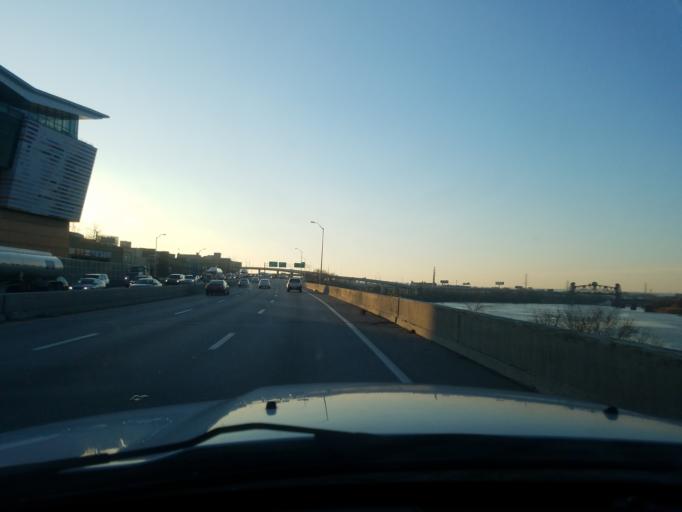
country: US
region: Kentucky
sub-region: Jefferson County
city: Louisville
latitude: 38.2590
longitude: -85.7592
